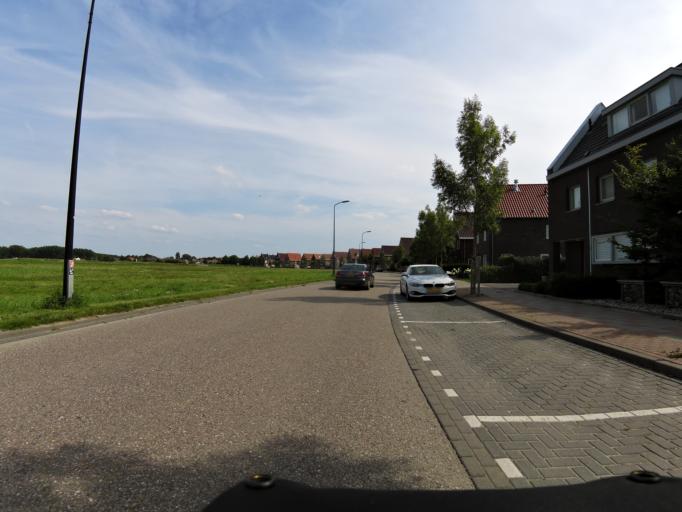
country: NL
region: South Holland
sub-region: Gemeente Goeree-Overflakkee
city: Middelharnis
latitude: 51.7636
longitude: 4.1578
